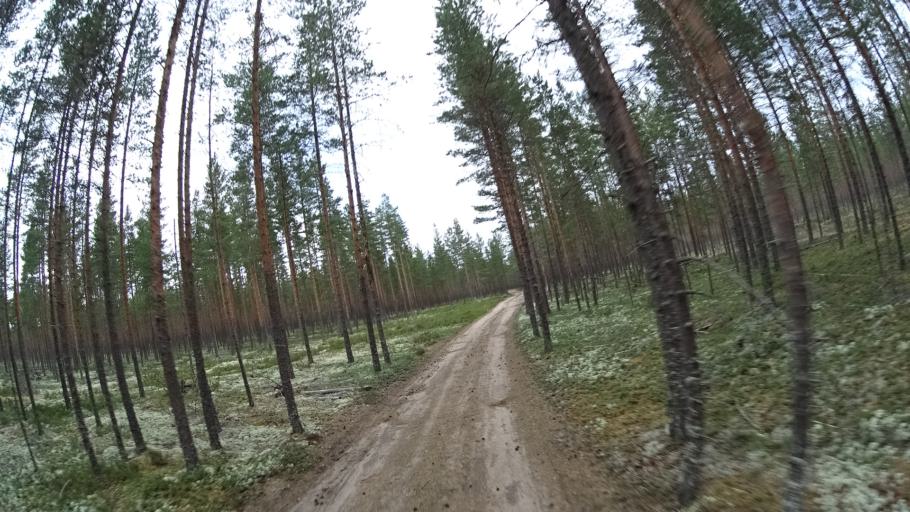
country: FI
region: Satakunta
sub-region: Pohjois-Satakunta
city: Jaemijaervi
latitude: 61.7642
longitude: 22.7866
